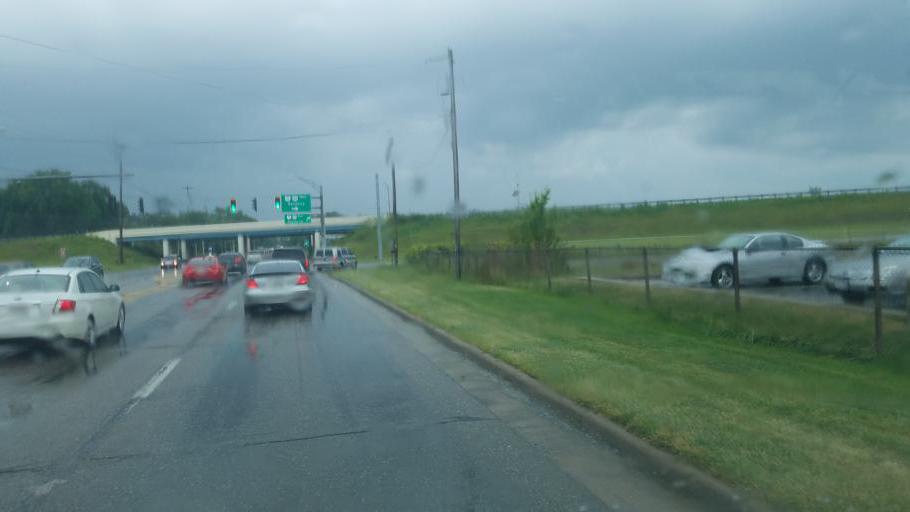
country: US
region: Ohio
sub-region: Trumbull County
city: Champion Heights
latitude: 41.2771
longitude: -80.8423
